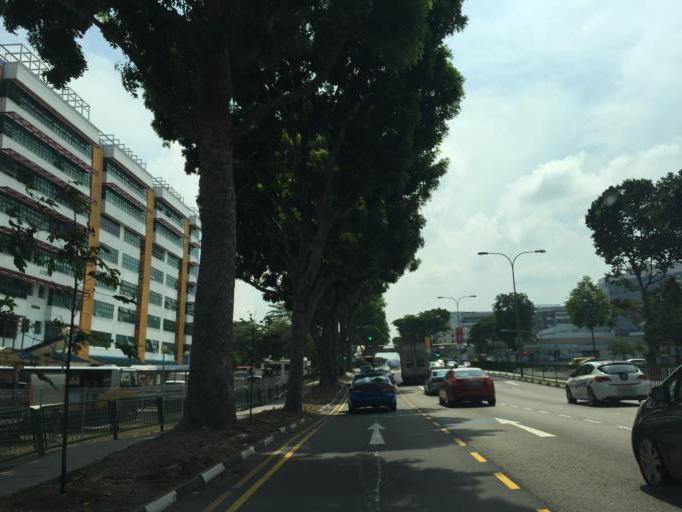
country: SG
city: Singapore
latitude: 1.3378
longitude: 103.9499
